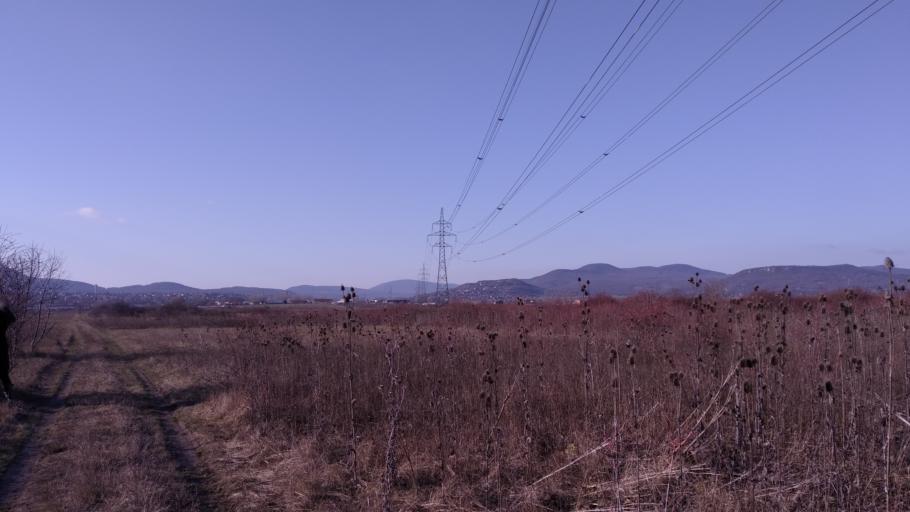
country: HU
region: Pest
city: Budakalasz
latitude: 47.6377
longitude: 19.0618
